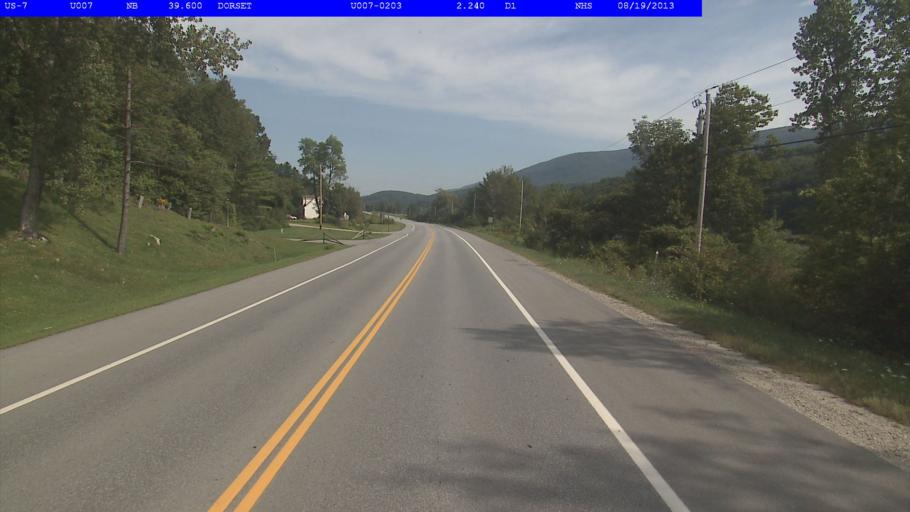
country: US
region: Vermont
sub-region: Bennington County
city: Manchester Center
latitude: 43.2413
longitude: -73.0095
